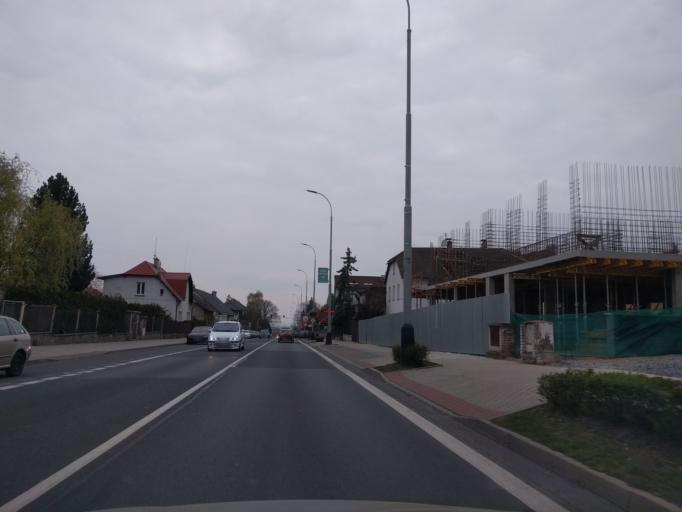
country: CZ
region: Central Bohemia
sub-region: Okres Praha-Vychod
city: Ricany
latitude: 49.9978
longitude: 14.6726
